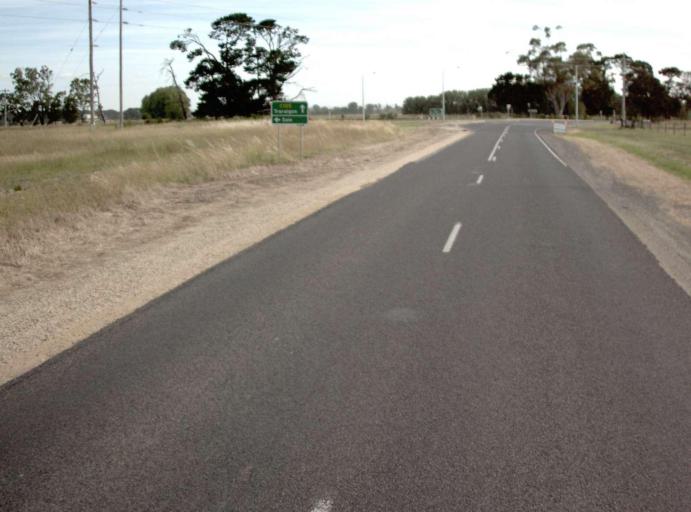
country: AU
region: Victoria
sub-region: Wellington
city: Heyfield
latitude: -38.0073
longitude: 146.7800
